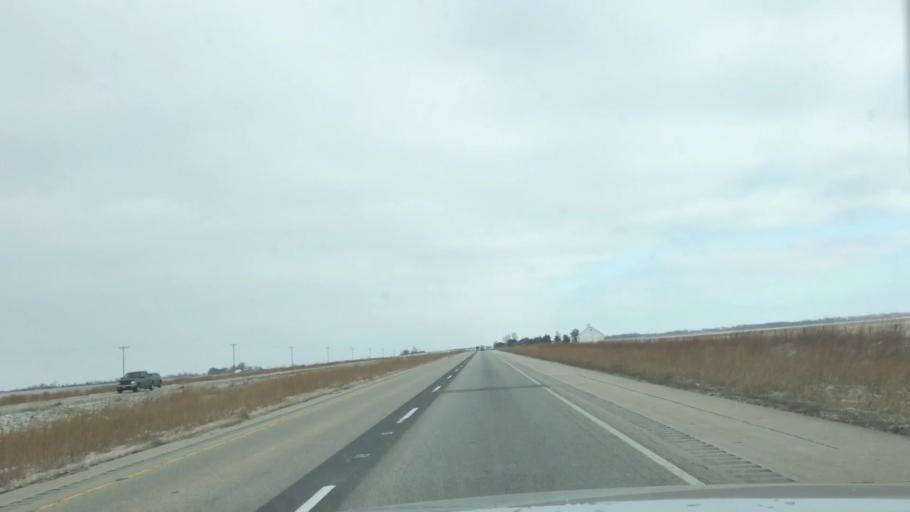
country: US
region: Illinois
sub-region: Sangamon County
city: Divernon
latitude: 39.4813
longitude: -89.6445
